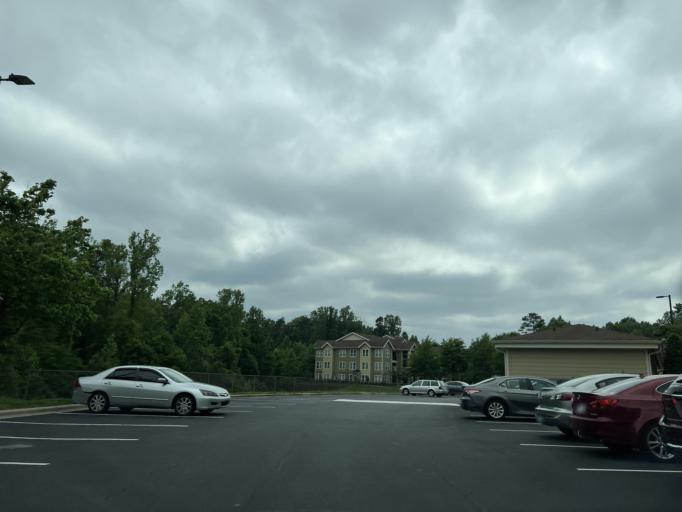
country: US
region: North Carolina
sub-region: Wake County
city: Raleigh
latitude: 35.8754
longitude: -78.5848
